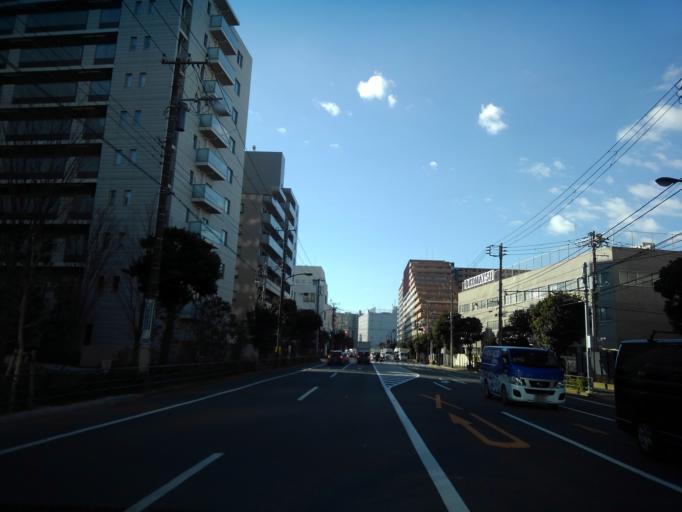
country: JP
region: Kanagawa
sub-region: Kawasaki-shi
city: Kawasaki
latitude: 35.6062
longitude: 139.7468
